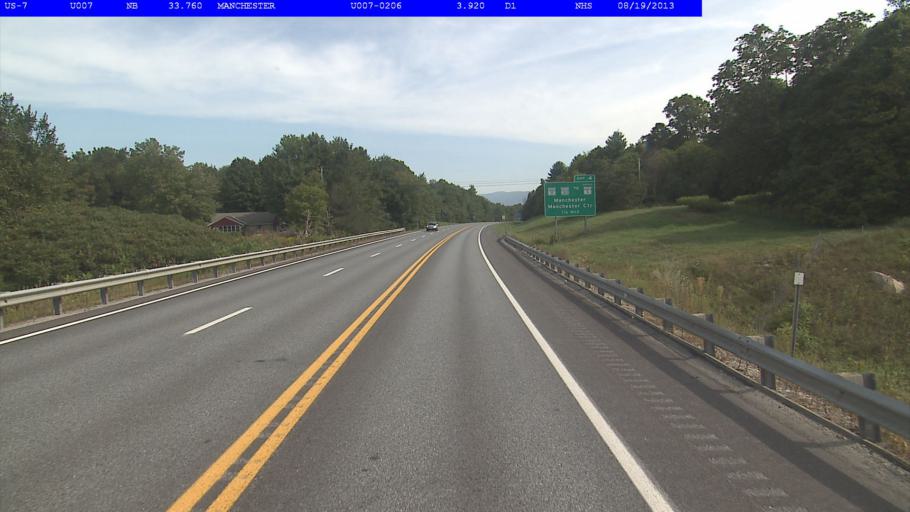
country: US
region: Vermont
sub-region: Bennington County
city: Manchester Center
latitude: 43.1654
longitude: -73.0400
